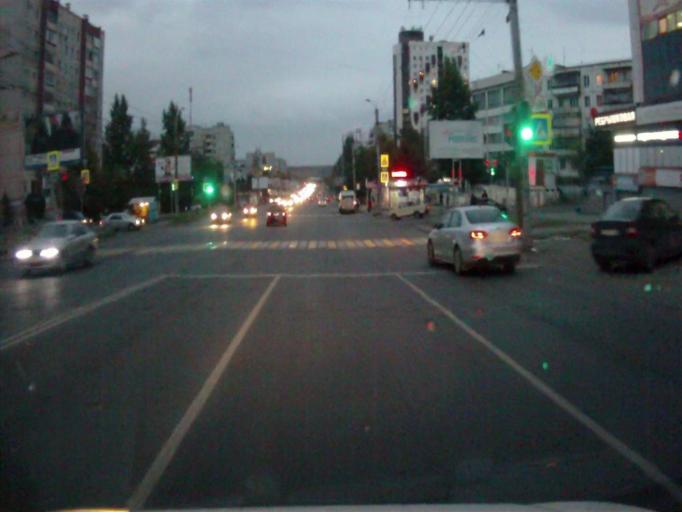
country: RU
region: Chelyabinsk
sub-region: Gorod Chelyabinsk
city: Chelyabinsk
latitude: 55.1845
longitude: 61.3326
